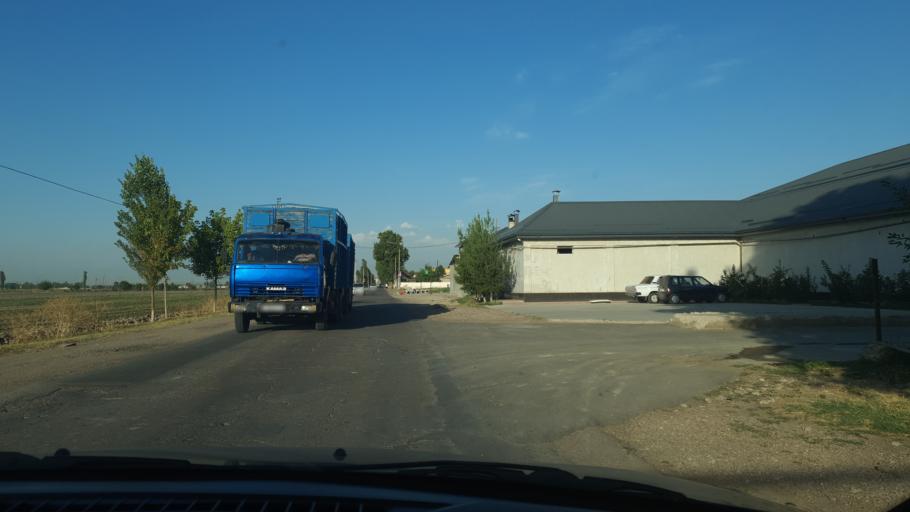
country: UZ
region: Toshkent
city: Tuytepa
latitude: 41.0846
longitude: 69.3355
